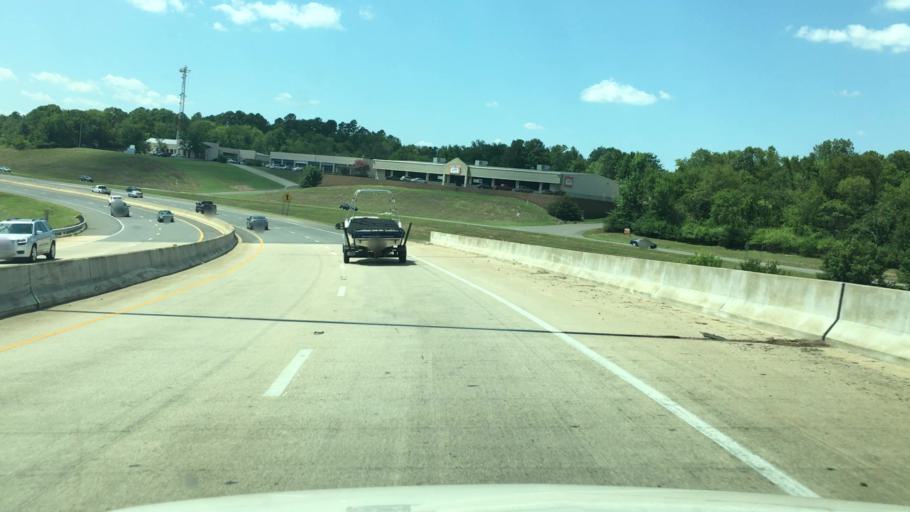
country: US
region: Arkansas
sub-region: Garland County
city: Rockwell
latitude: 34.4701
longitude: -93.0893
